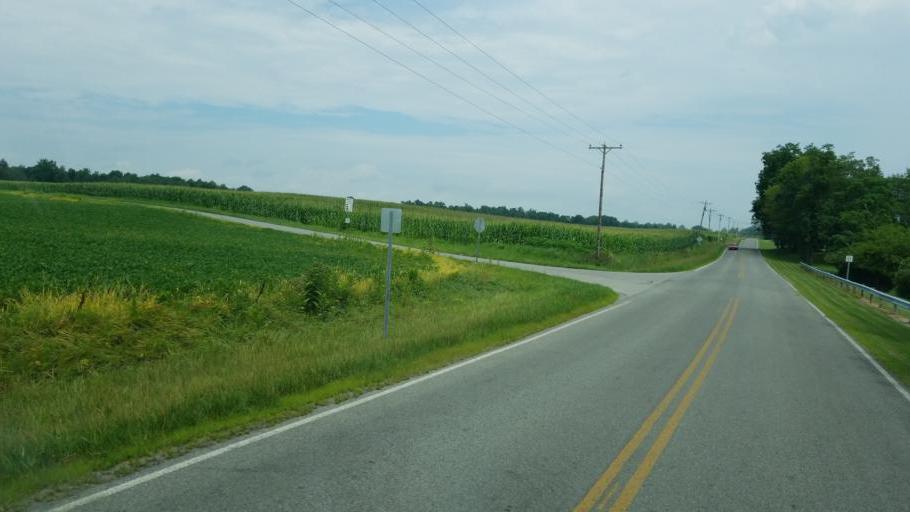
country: US
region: Ohio
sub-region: Logan County
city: Bellefontaine
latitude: 40.4133
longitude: -83.7756
